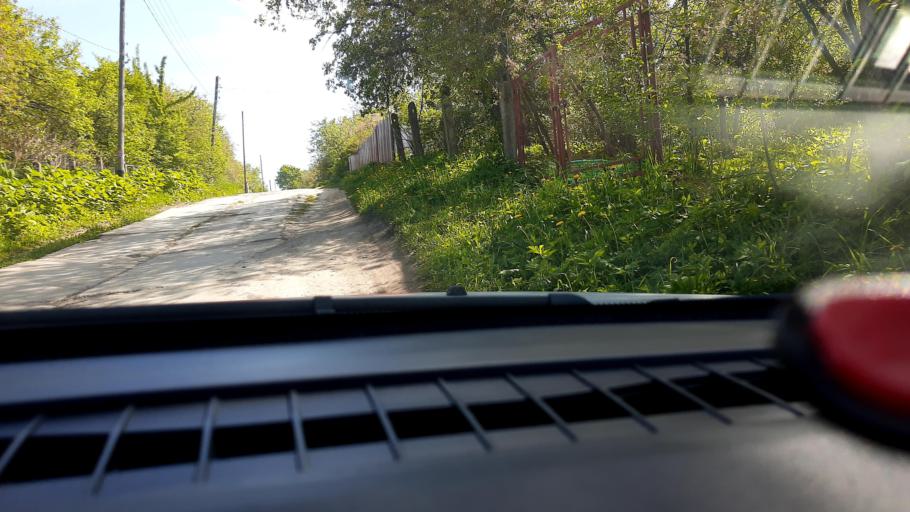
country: RU
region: Nizjnij Novgorod
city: Nizhniy Novgorod
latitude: 56.2297
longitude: 43.9645
